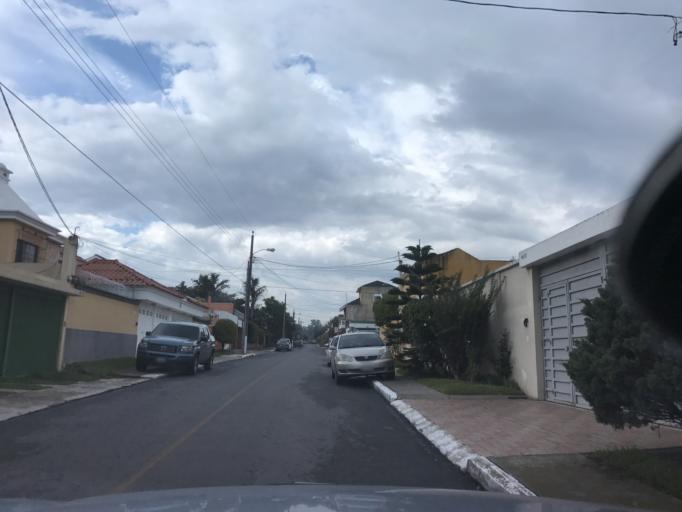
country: GT
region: Guatemala
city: Santa Catarina Pinula
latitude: 14.5777
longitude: -90.5530
